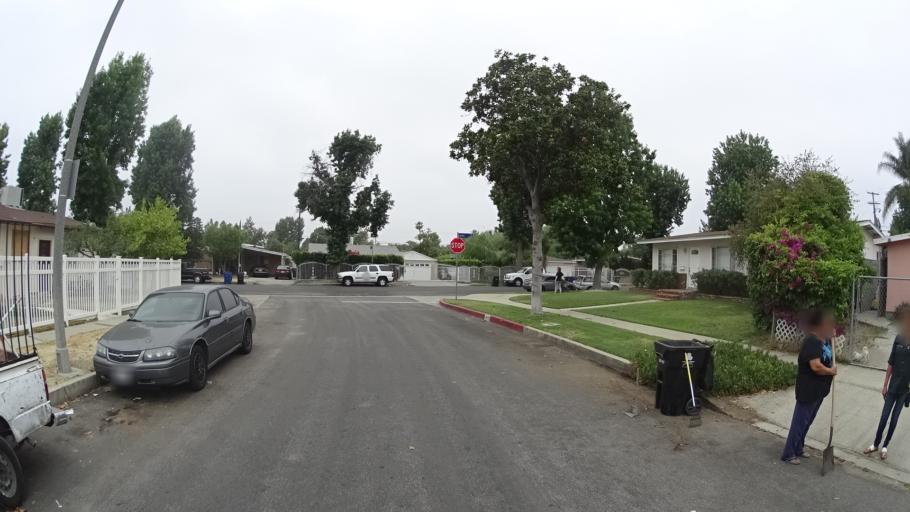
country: US
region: California
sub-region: Los Angeles County
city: Van Nuys
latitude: 34.1929
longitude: -118.4205
